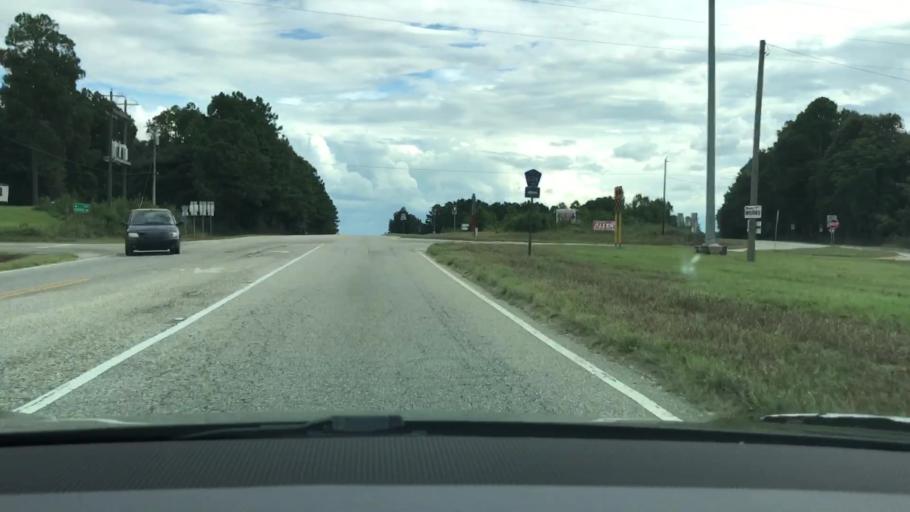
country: US
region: Alabama
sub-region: Pike County
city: Troy
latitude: 31.6780
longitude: -85.9574
